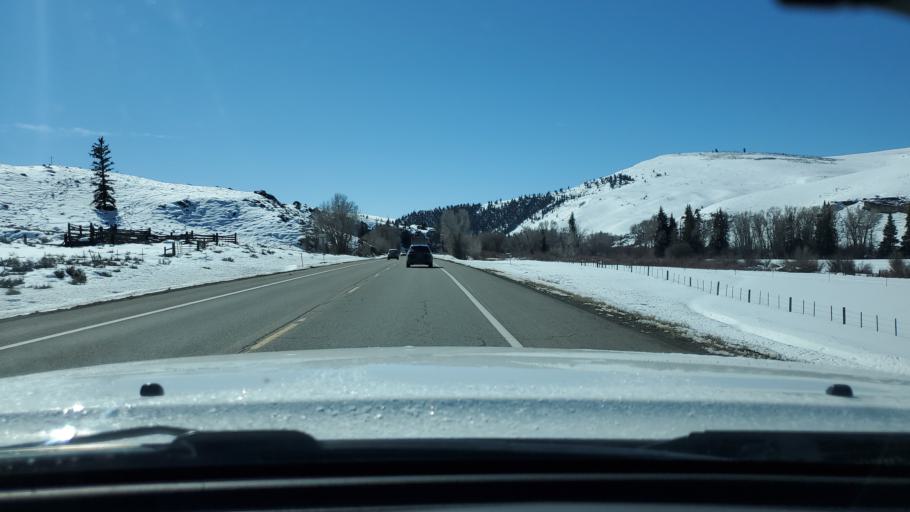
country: US
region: Colorado
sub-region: Gunnison County
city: Gunnison
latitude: 38.6872
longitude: -106.8522
